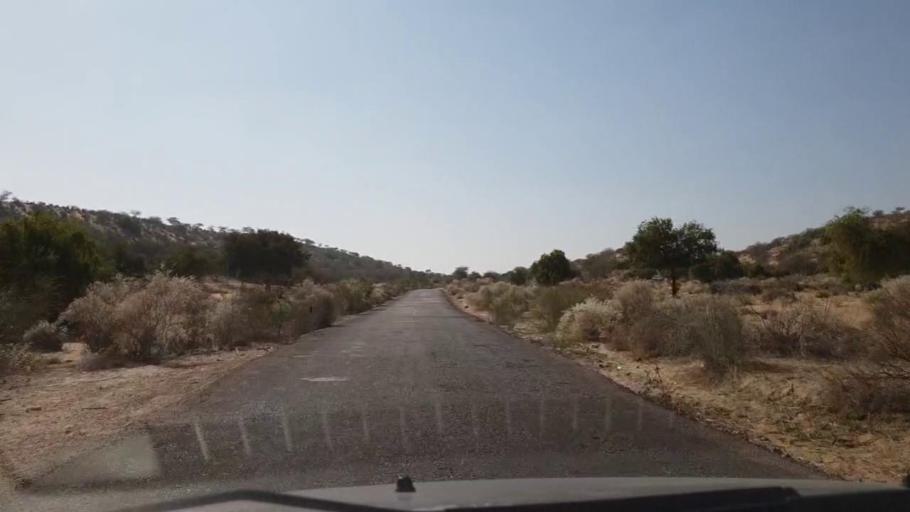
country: PK
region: Sindh
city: Mithi
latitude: 24.6780
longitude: 69.7760
